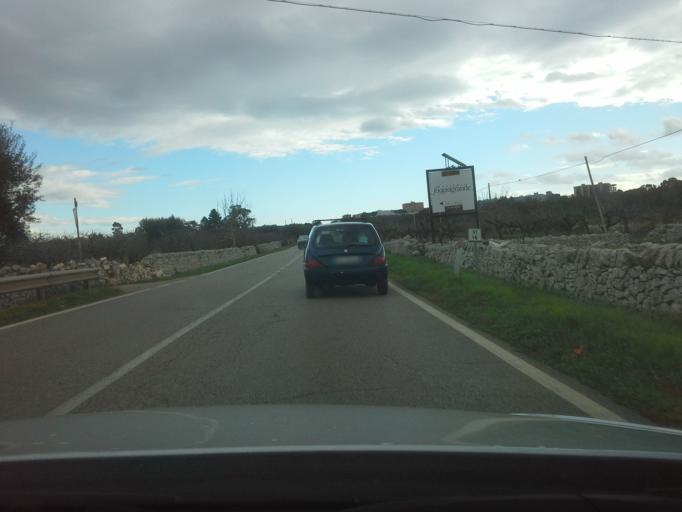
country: IT
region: Apulia
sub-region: Provincia di Bari
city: Putignano
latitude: 40.8737
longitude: 17.0793
